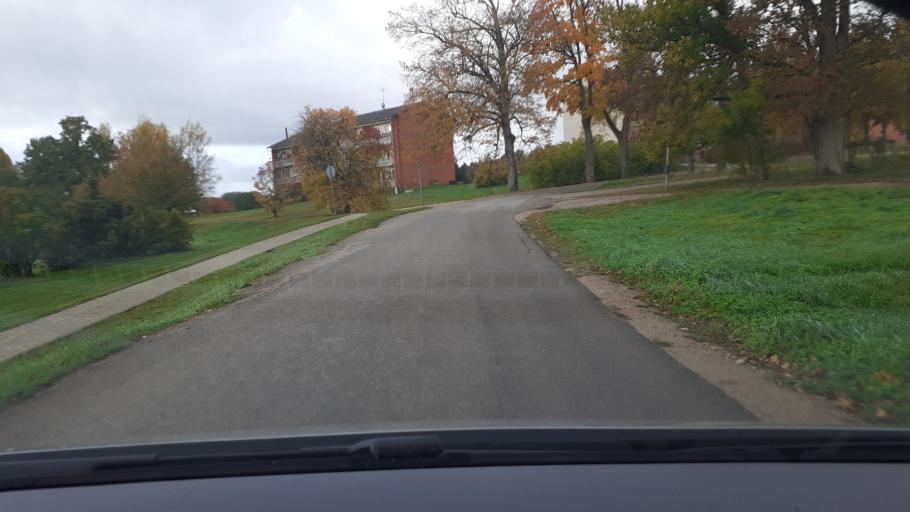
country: LV
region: Kuldigas Rajons
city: Kuldiga
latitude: 57.0178
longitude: 21.9086
